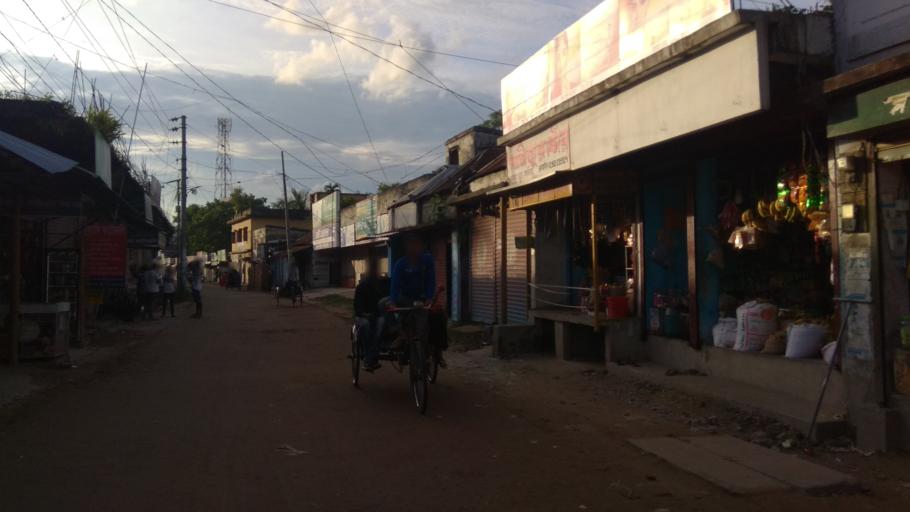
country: BD
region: Khulna
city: Kalia
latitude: 23.0392
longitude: 89.6322
